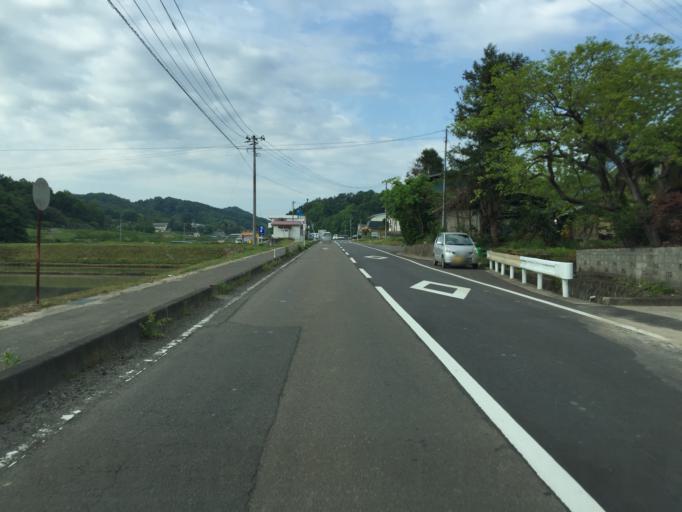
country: JP
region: Fukushima
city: Hobaramachi
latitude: 37.7267
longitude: 140.5982
